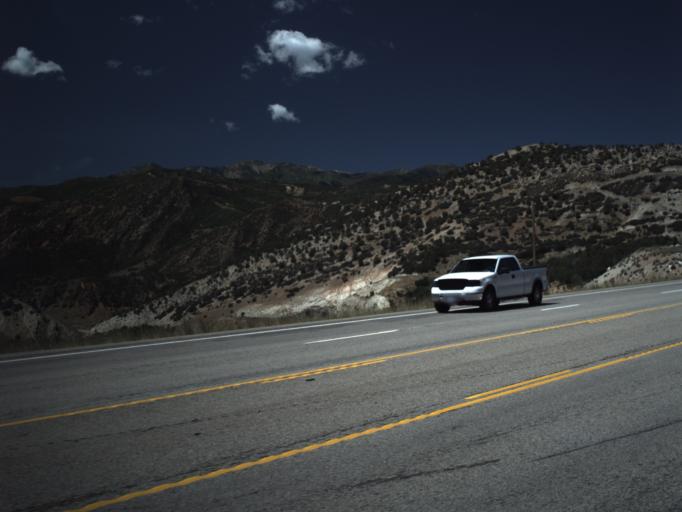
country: US
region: Utah
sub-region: Utah County
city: Mapleton
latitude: 39.9987
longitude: -111.4782
